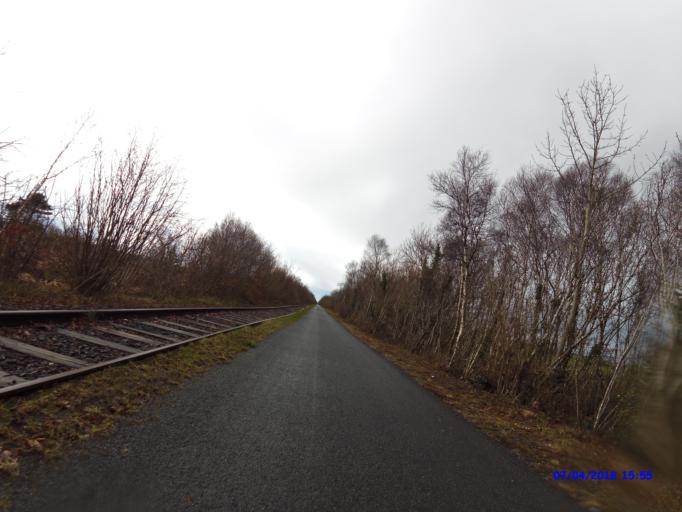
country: IE
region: Leinster
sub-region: An Iarmhi
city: Athlone
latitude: 53.4177
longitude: -7.8735
